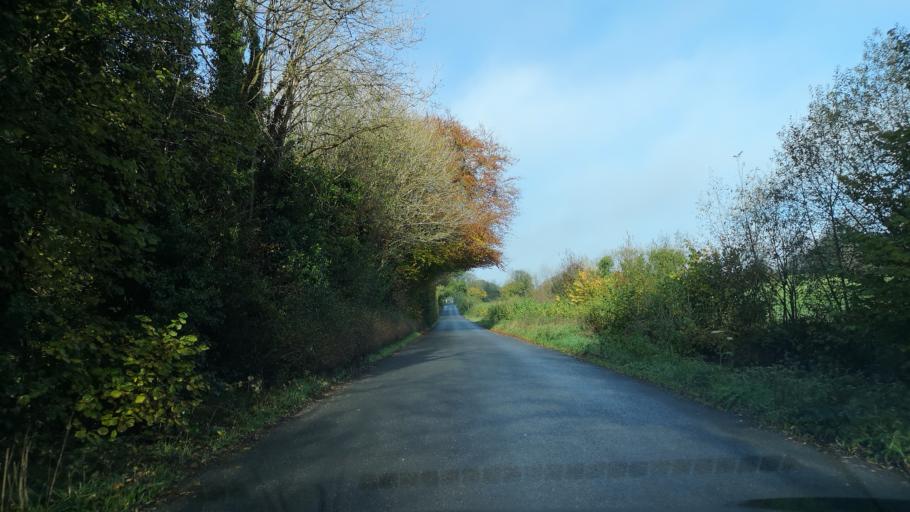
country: IE
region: Leinster
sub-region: An Iarmhi
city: Moate
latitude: 53.3862
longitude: -7.8056
